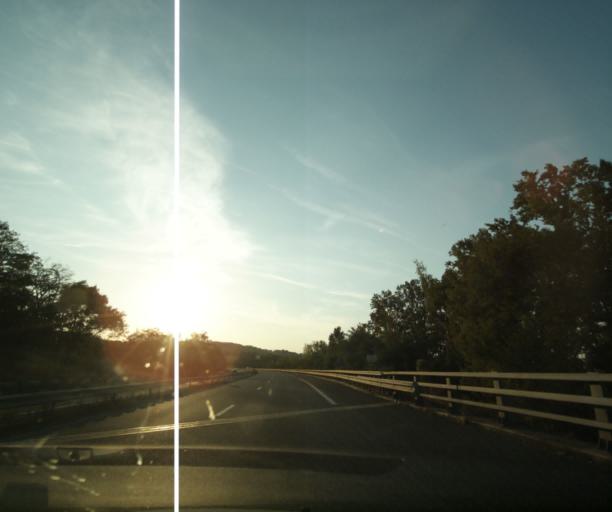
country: FR
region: Aquitaine
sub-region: Departement du Lot-et-Garonne
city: Layrac
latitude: 44.1428
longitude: 0.6609
